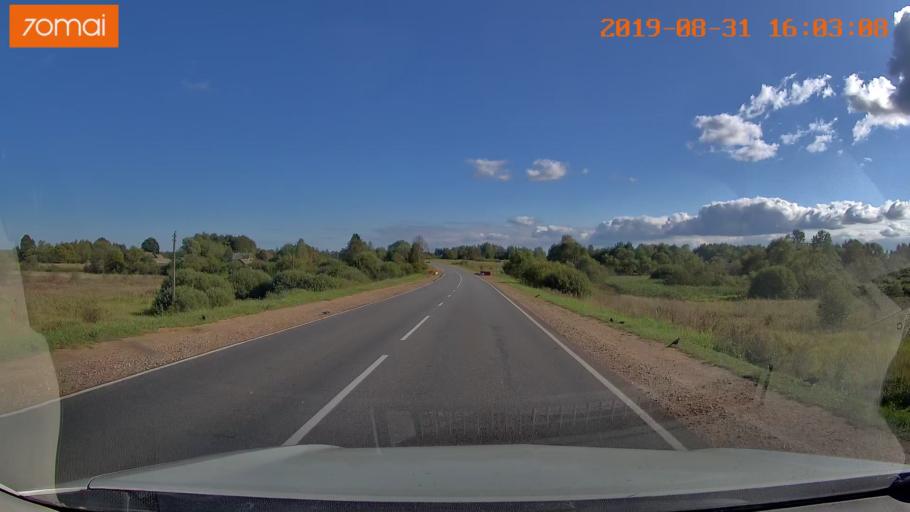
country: RU
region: Kaluga
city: Yukhnov
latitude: 54.6678
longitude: 35.3102
